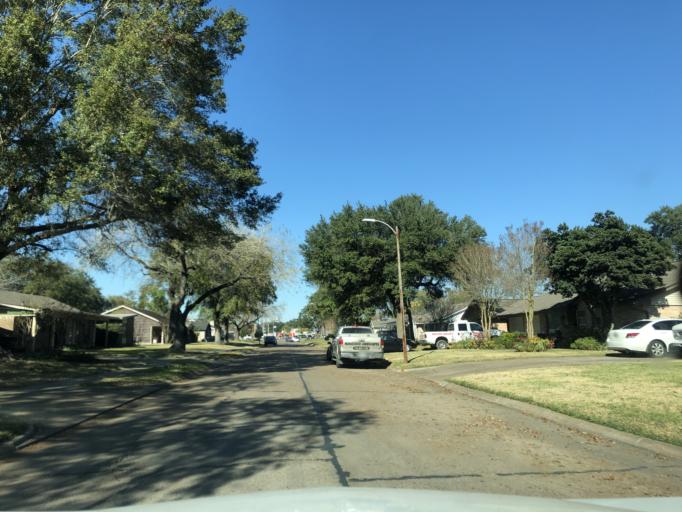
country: US
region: Texas
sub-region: Harris County
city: Bellaire
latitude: 29.6864
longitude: -95.5037
